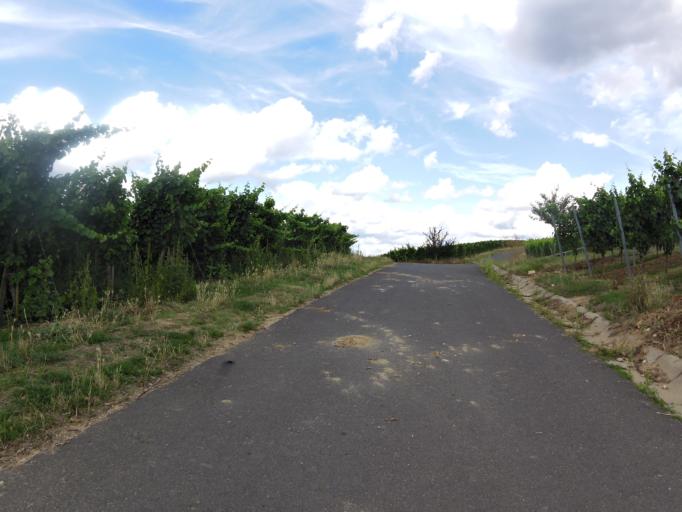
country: DE
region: Bavaria
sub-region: Regierungsbezirk Unterfranken
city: Sommerhausen
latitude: 49.6863
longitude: 10.0316
